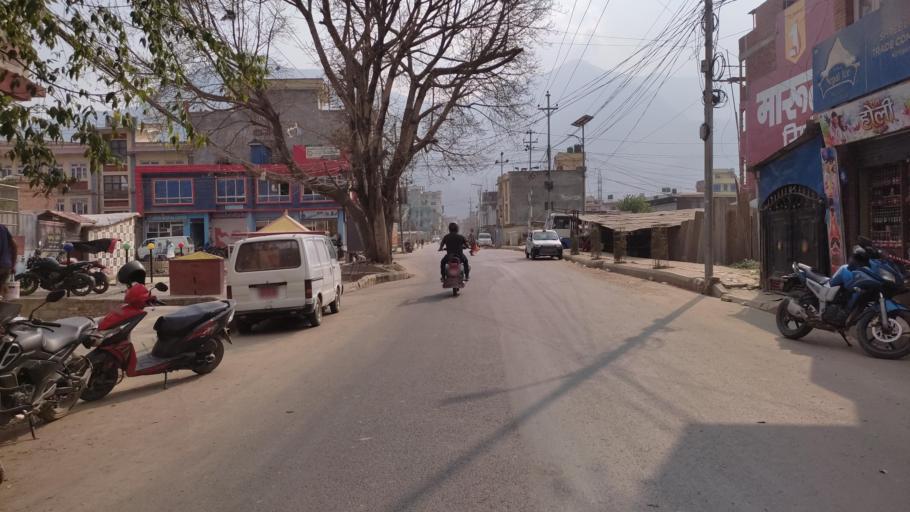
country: NP
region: Central Region
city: Kirtipur
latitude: 27.6706
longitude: 85.2710
